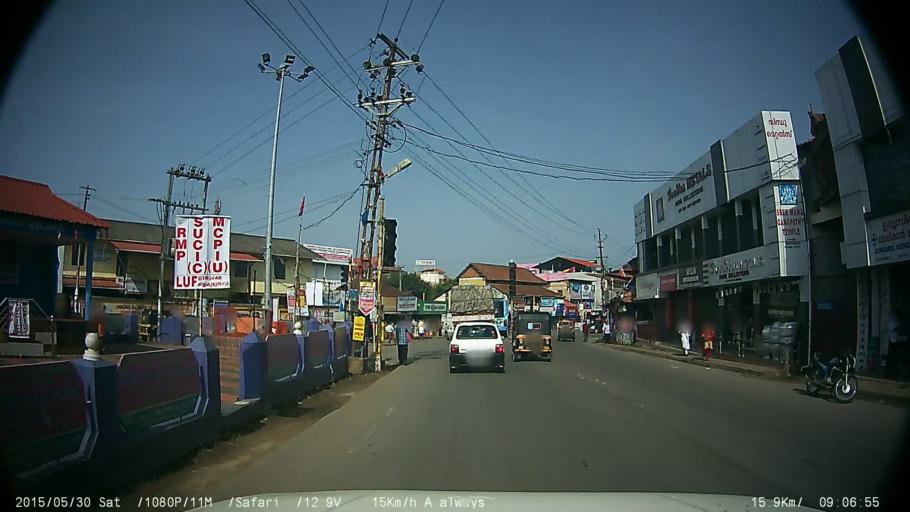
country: IN
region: Kerala
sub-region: Wayanad
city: Panamaram
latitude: 11.6631
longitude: 76.2577
